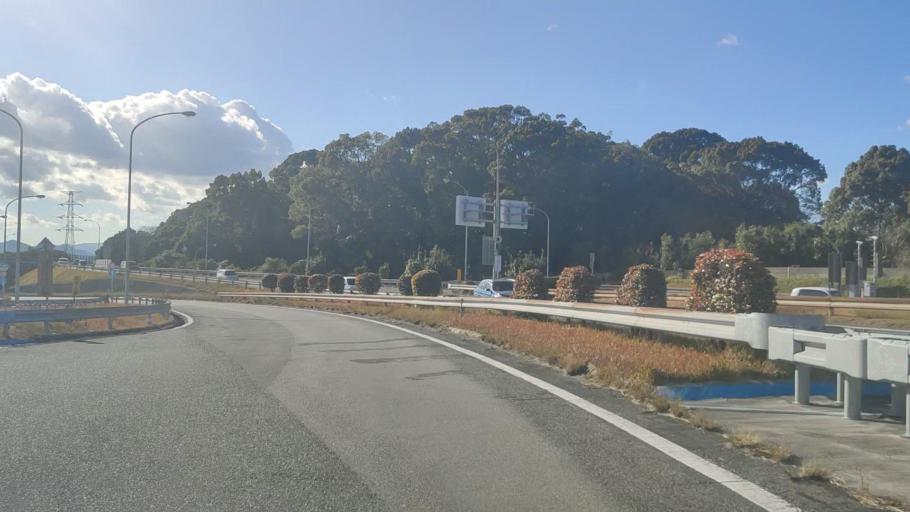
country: JP
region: Fukuoka
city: Nogata
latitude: 33.7821
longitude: 130.7438
